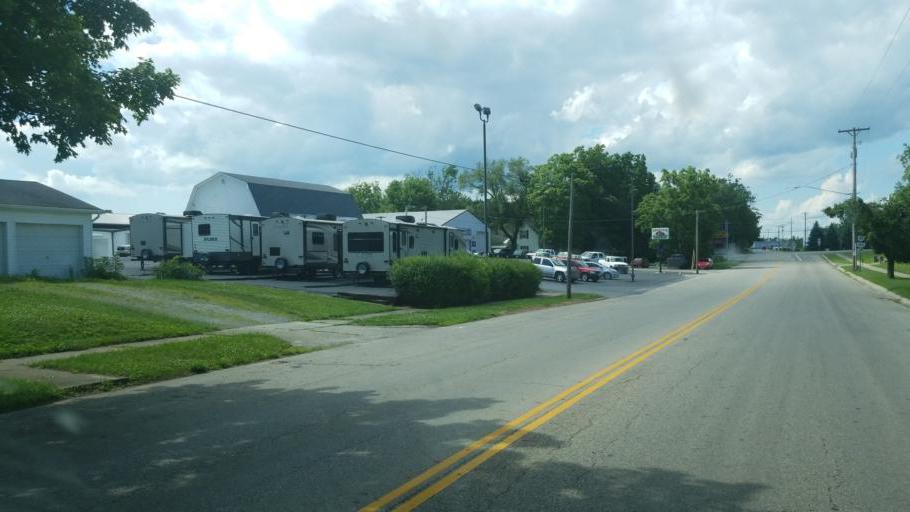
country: US
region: Ohio
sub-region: Highland County
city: Greenfield
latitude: 39.3585
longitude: -83.3855
